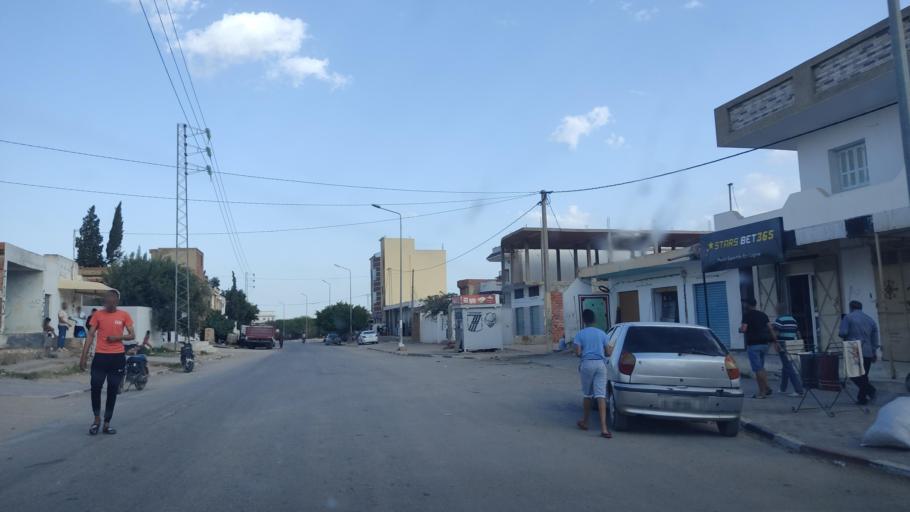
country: TN
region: Safaqis
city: Sfax
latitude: 34.8448
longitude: 10.6175
